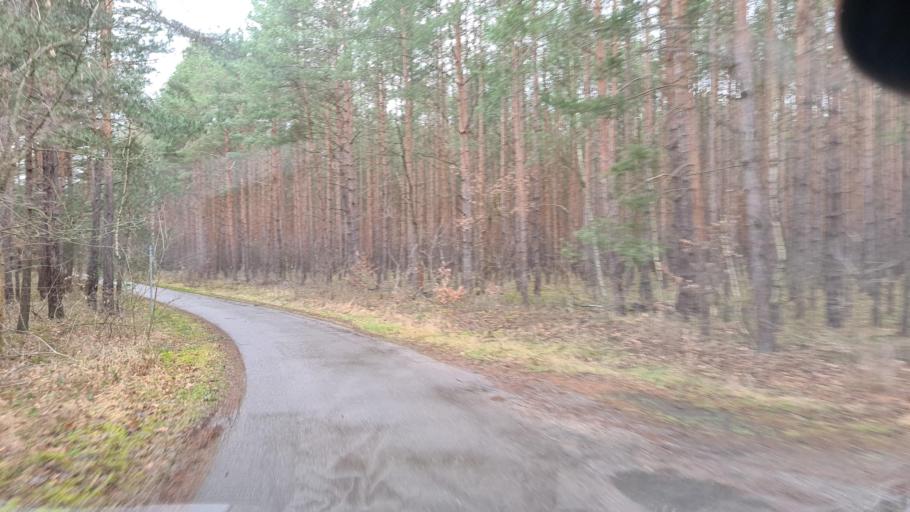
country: DE
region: Brandenburg
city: Kroppen
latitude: 51.4059
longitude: 13.7821
